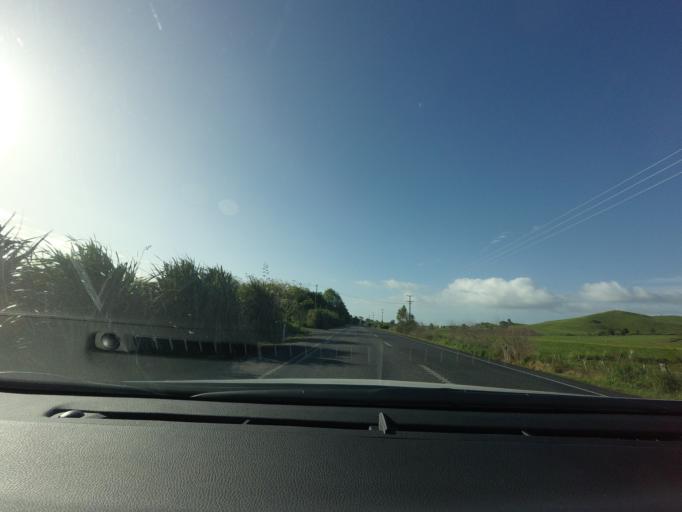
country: NZ
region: Waikato
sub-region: Hauraki District
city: Ngatea
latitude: -37.4511
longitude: 175.5086
